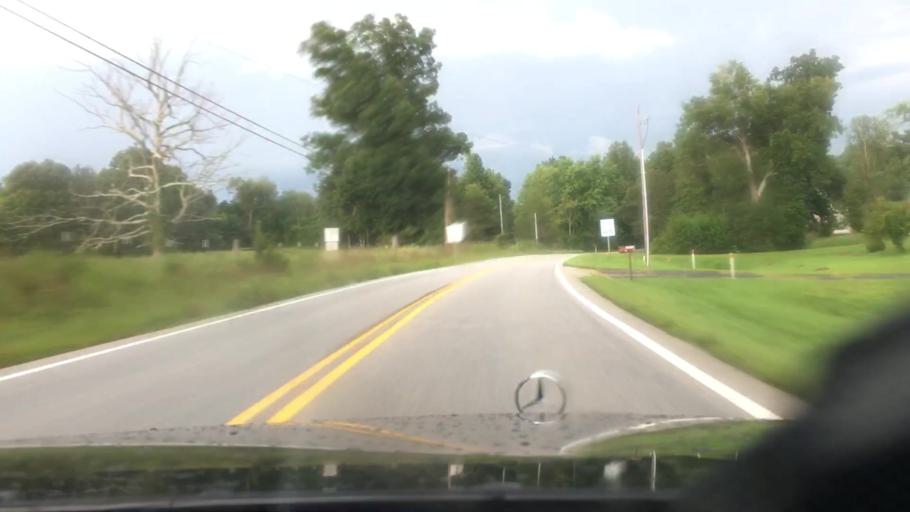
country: US
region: Virginia
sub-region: Nelson County
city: Lovingston
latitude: 37.7683
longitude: -78.9792
